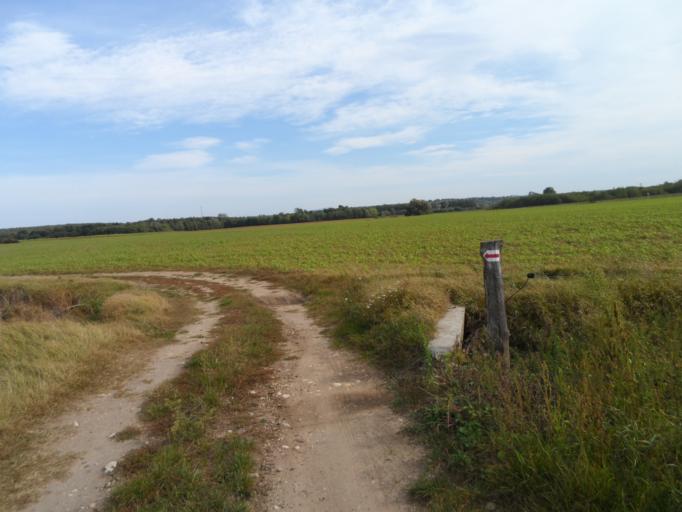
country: HU
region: Veszprem
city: Papa
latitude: 47.2364
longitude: 17.5031
